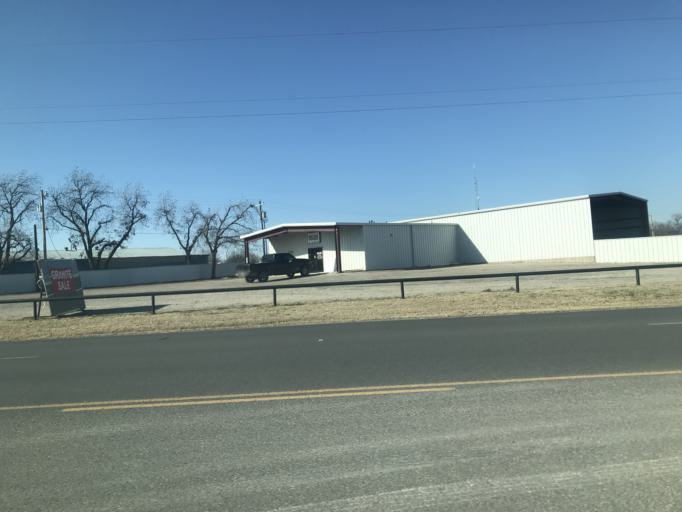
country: US
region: Texas
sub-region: Taylor County
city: Abilene
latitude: 32.4214
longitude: -99.7372
